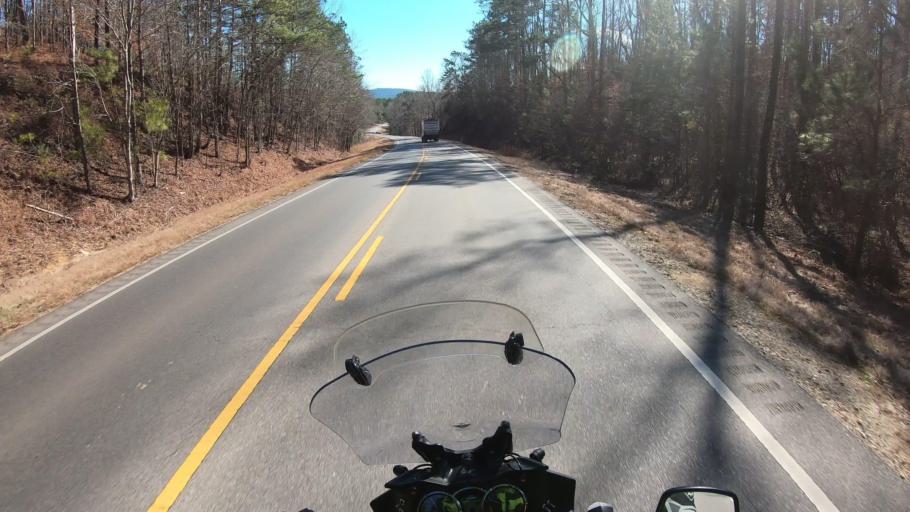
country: US
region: Alabama
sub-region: Cleburne County
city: Heflin
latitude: 33.5684
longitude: -85.6148
